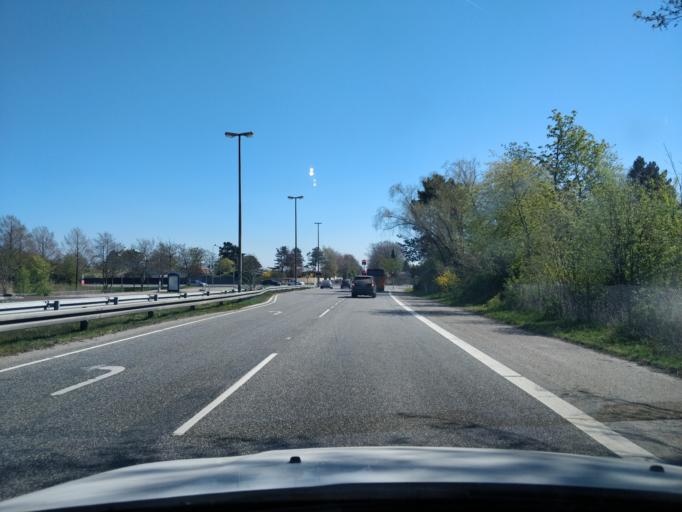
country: DK
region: Capital Region
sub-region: Ishoj Kommune
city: Ishoj
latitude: 55.6130
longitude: 12.3640
